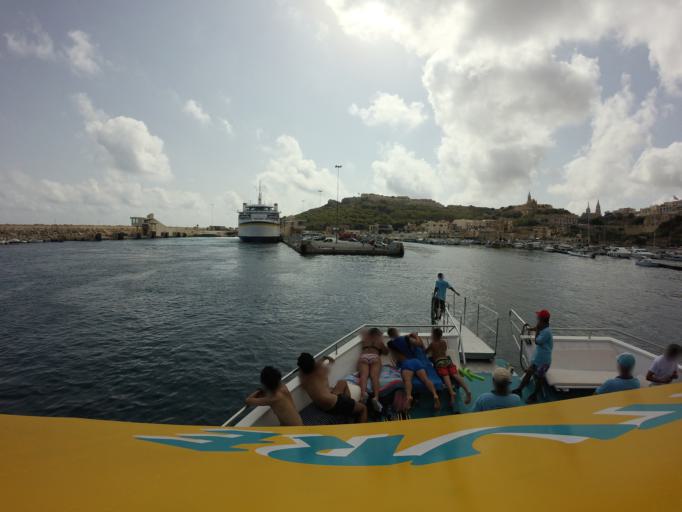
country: MT
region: Ghajnsielem
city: Mgarr
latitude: 36.0254
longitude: 14.2997
